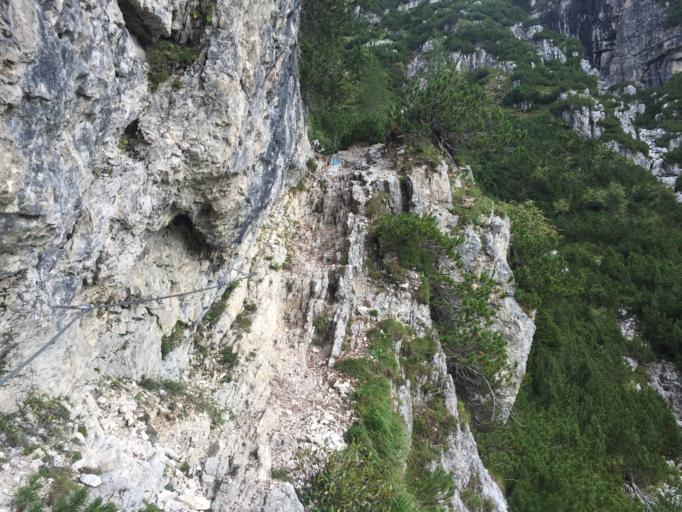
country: SI
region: Bovec
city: Bovec
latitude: 46.4198
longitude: 13.5033
